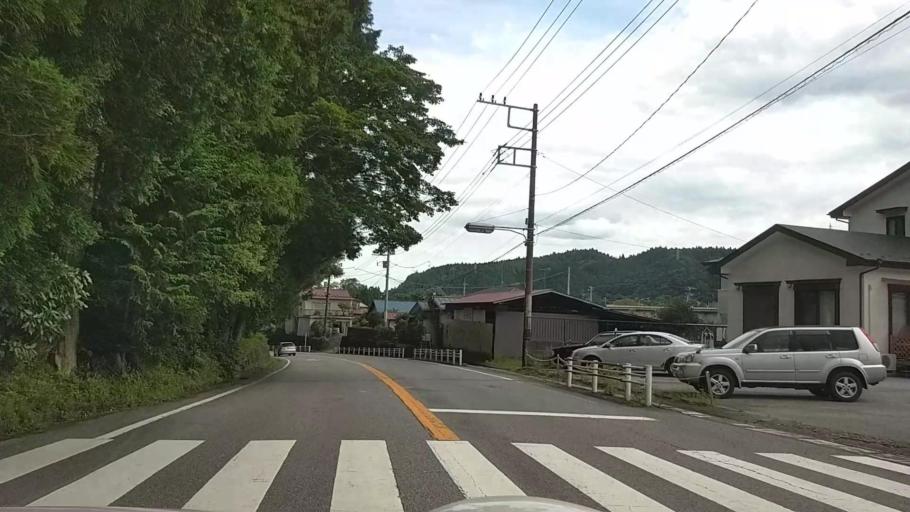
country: JP
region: Tochigi
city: Nikko
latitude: 36.7455
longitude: 139.6238
